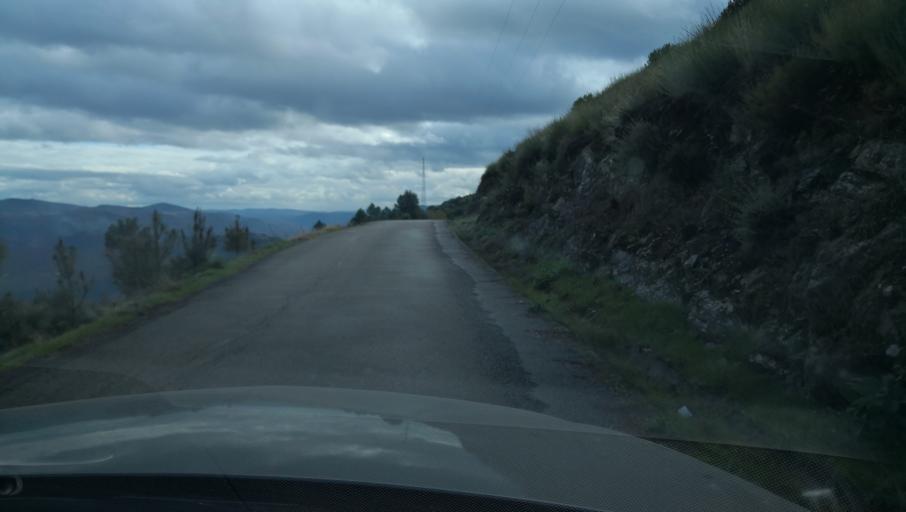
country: PT
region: Vila Real
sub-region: Sabrosa
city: Vilela
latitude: 41.1937
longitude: -7.5719
